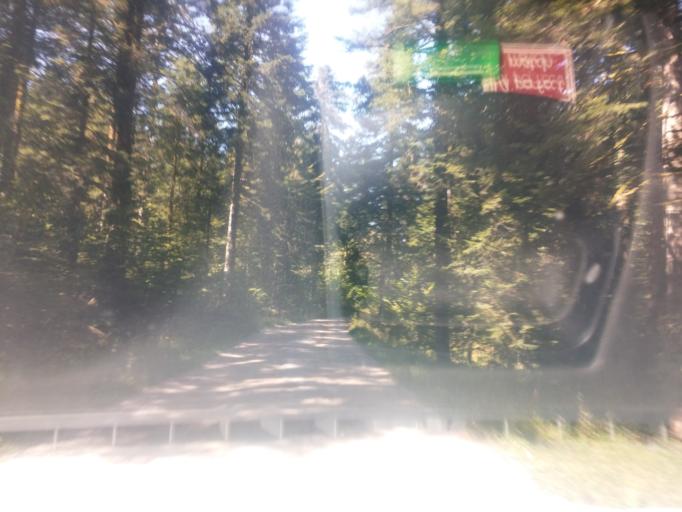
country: FR
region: Franche-Comte
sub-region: Departement du Jura
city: Saint-Lupicin
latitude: 46.4201
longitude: 5.7792
